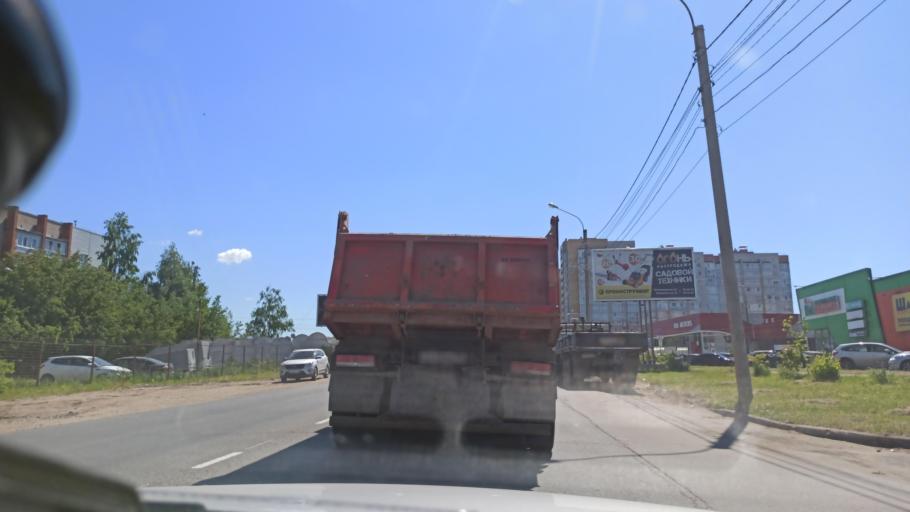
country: RU
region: Vologda
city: Vologda
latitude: 59.1946
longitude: 39.8292
